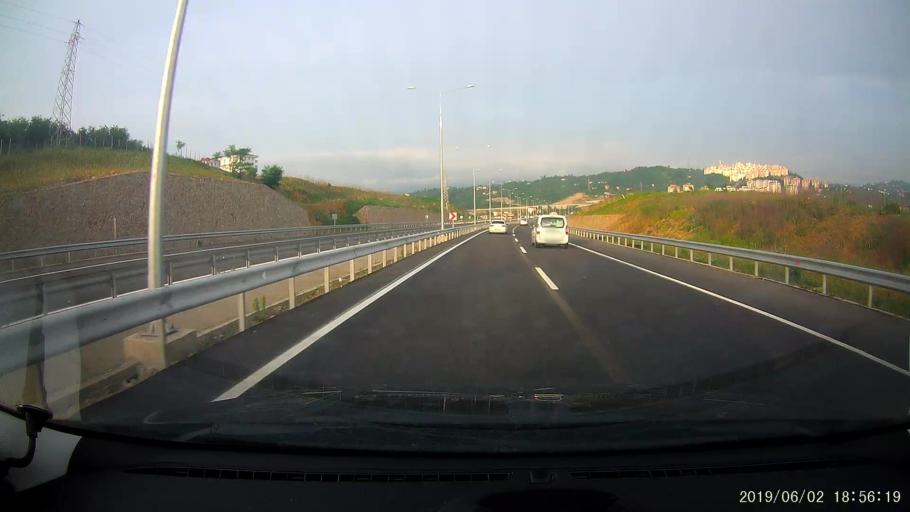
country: TR
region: Ordu
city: Ordu
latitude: 40.9560
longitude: 37.8880
